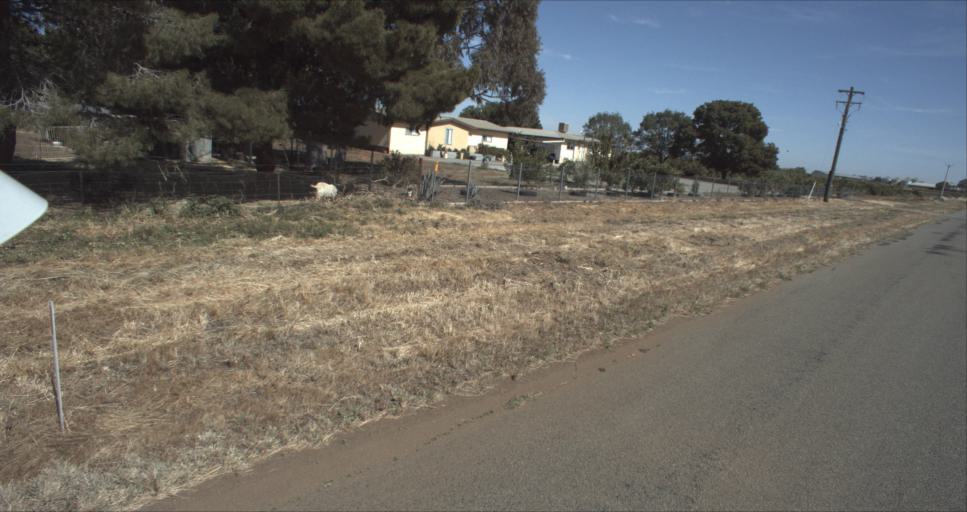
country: AU
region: New South Wales
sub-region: Leeton
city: Leeton
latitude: -34.5640
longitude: 146.4704
